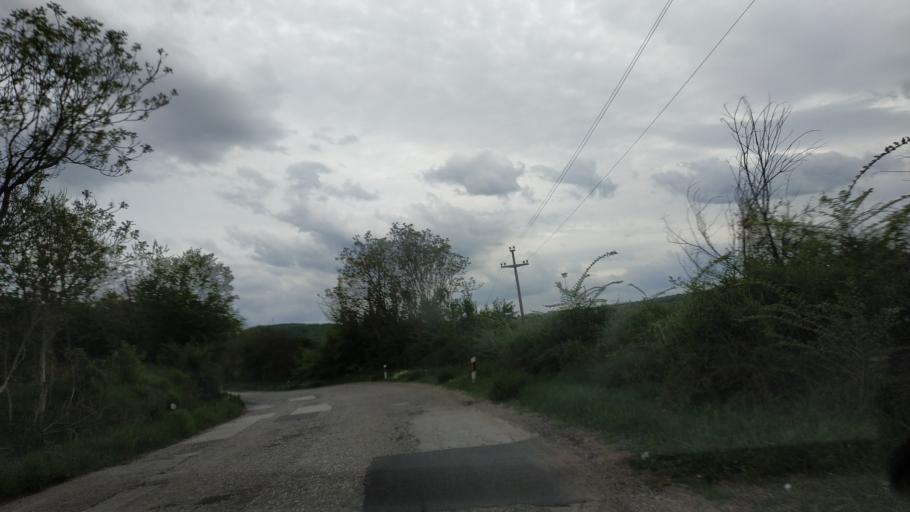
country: RS
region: Central Serbia
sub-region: Nisavski Okrug
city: Aleksinac
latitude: 43.6015
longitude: 21.6865
